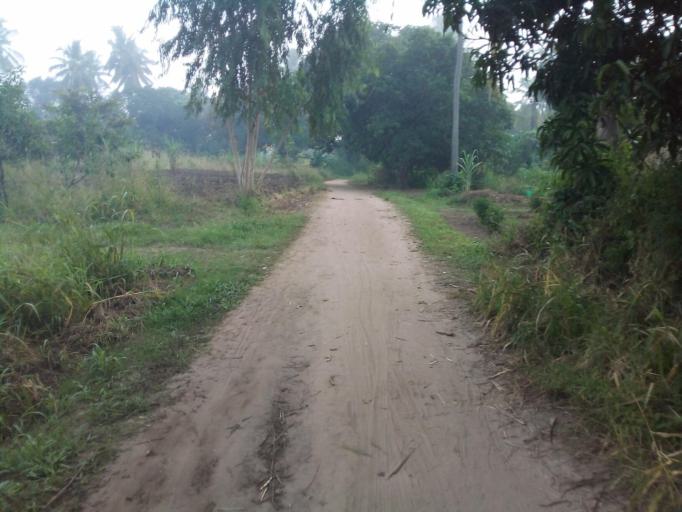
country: MZ
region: Zambezia
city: Quelimane
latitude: -17.5890
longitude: 36.6847
